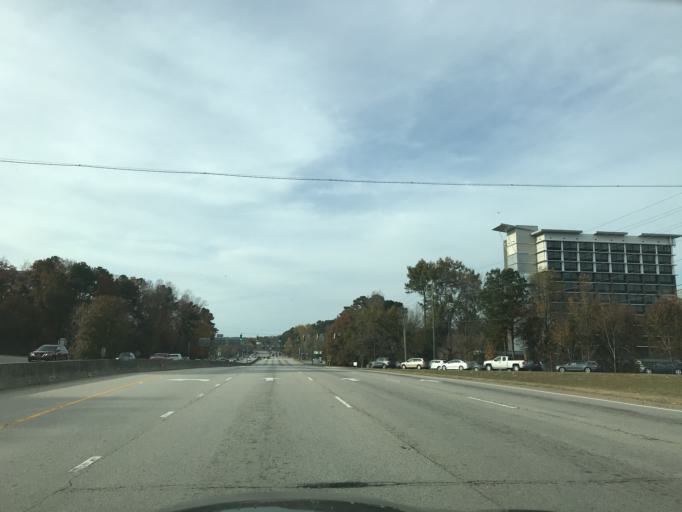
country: US
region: North Carolina
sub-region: Wake County
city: West Raleigh
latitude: 35.8357
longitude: -78.6698
